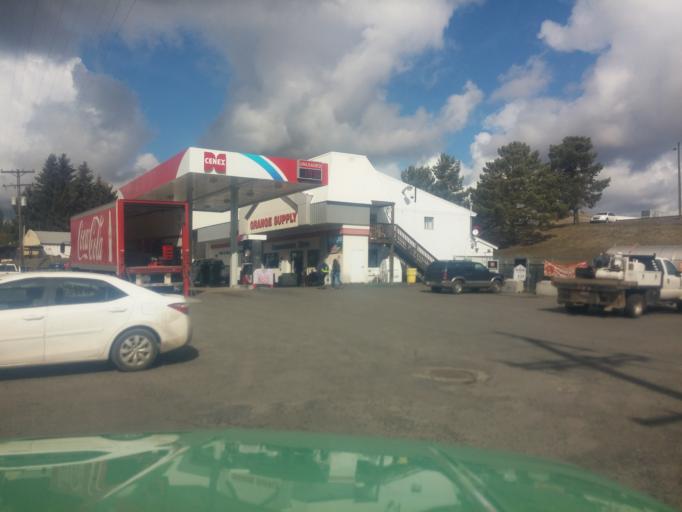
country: US
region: Idaho
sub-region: Latah County
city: Moscow
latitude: 46.9269
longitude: -116.9044
